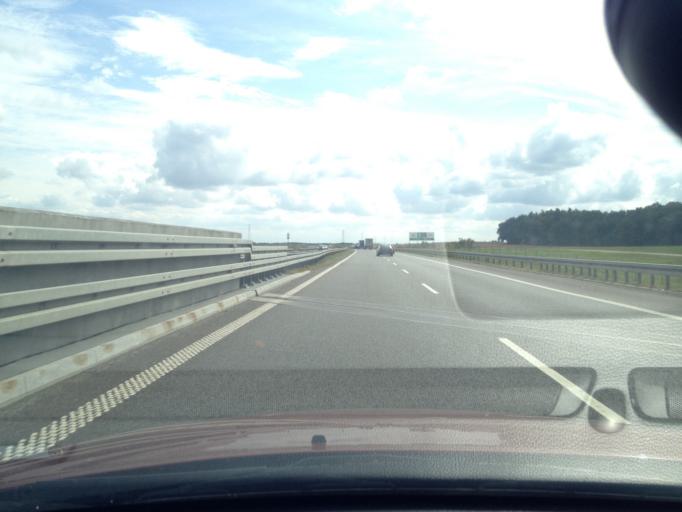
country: PL
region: West Pomeranian Voivodeship
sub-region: Powiat gryfinski
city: Gryfino
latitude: 53.3195
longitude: 14.5761
